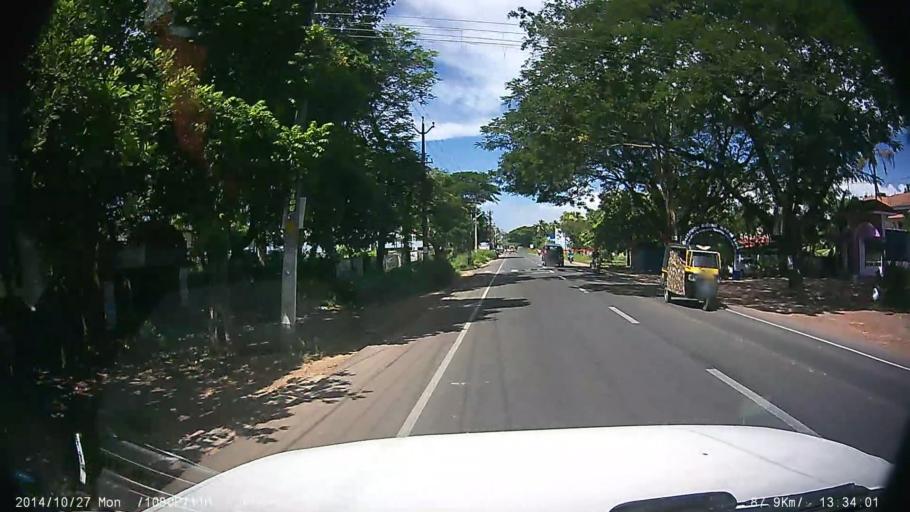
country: IN
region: Kerala
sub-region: Alappuzha
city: Alleppey
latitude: 9.5800
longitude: 76.3275
